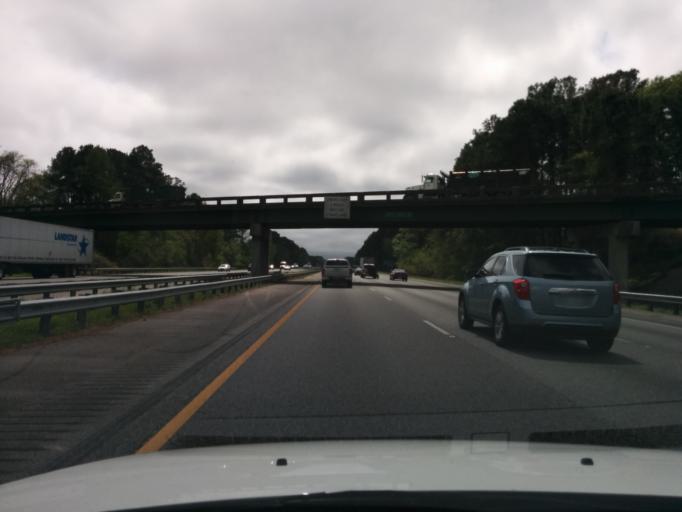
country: US
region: Georgia
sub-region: Chatham County
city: Georgetown
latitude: 32.0283
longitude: -81.2692
